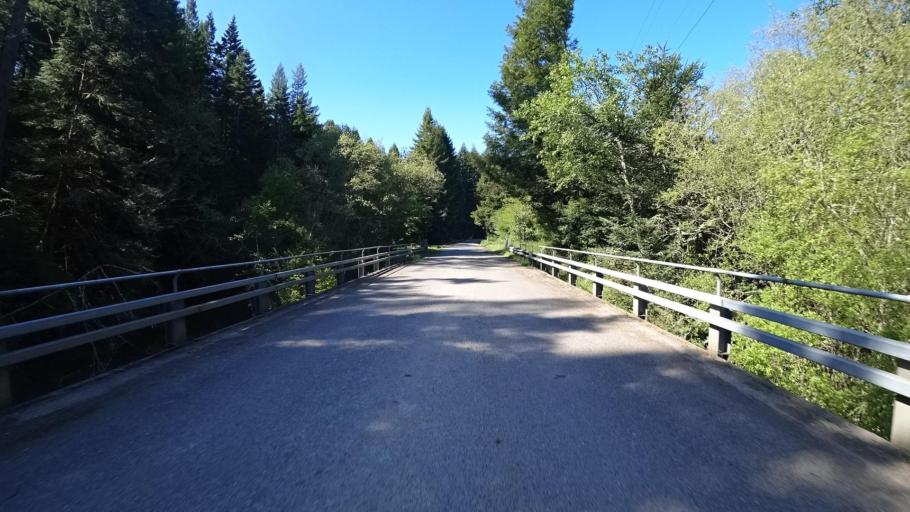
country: US
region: California
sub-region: Humboldt County
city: Fortuna
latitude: 40.5254
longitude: -124.1897
